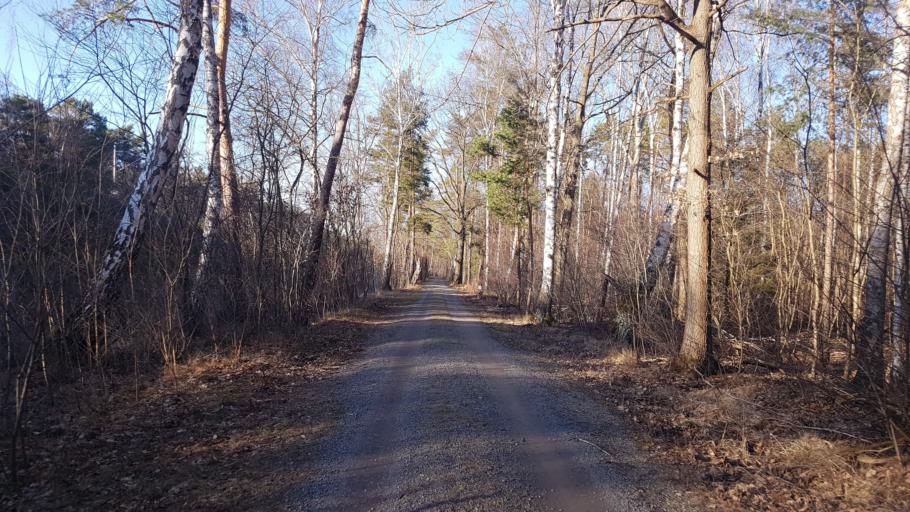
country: DE
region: Brandenburg
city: Hohenleipisch
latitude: 51.5116
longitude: 13.5768
